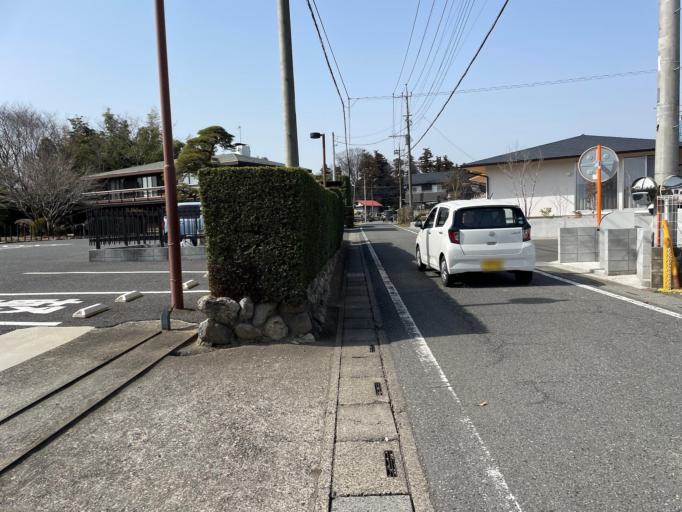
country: JP
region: Saitama
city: Yorii
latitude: 36.1107
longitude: 139.2436
